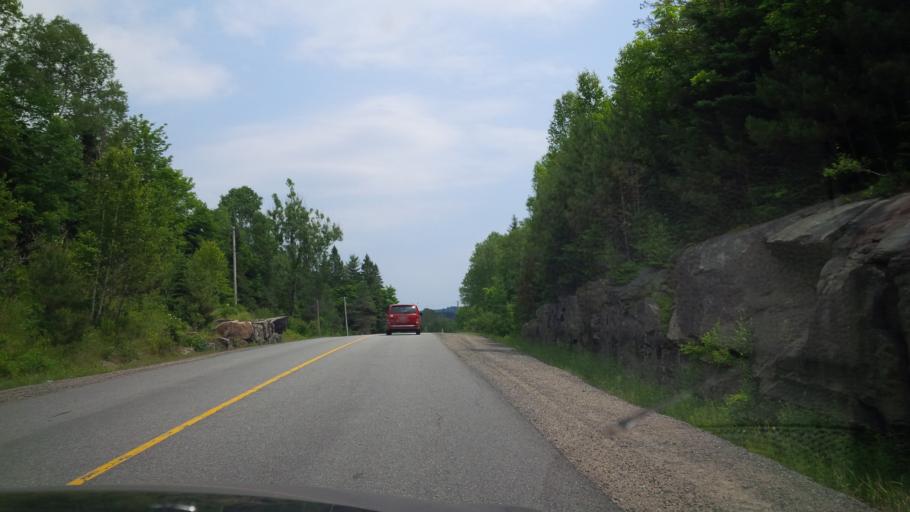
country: CA
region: Ontario
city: Huntsville
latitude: 45.5509
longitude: -79.2377
